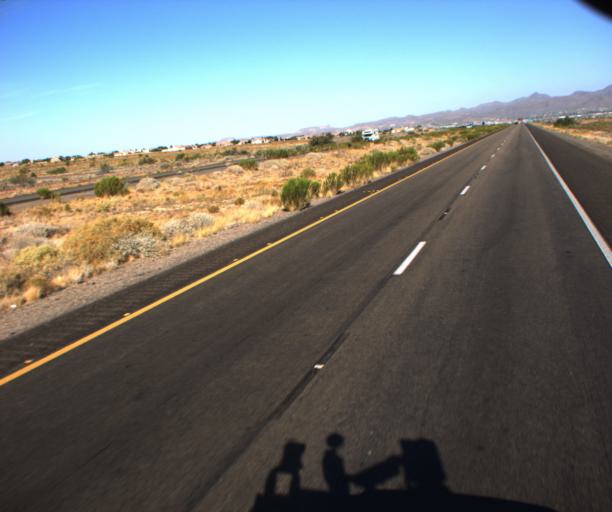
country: US
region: Arizona
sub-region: Mohave County
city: New Kingman-Butler
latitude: 35.2091
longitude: -113.9604
